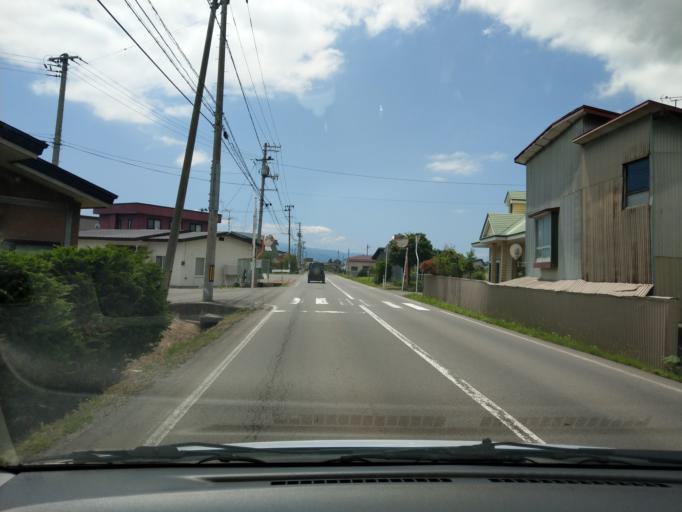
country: JP
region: Aomori
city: Kuroishi
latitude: 40.6350
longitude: 140.5653
